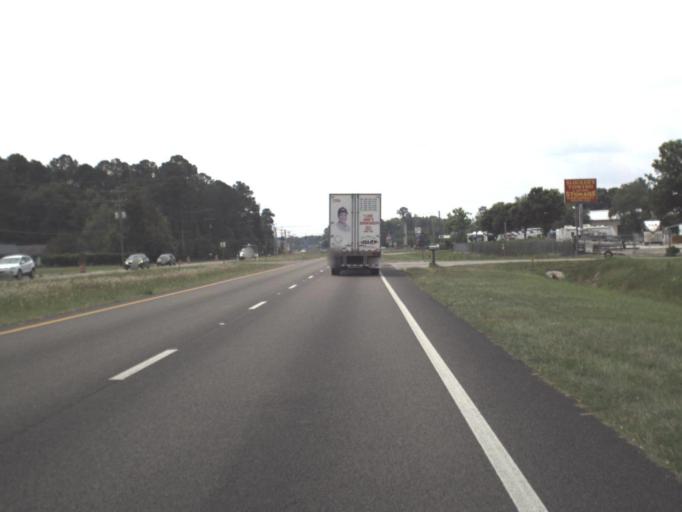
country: US
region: Florida
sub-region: Clay County
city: Green Cove Springs
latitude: 30.0273
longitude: -81.7075
